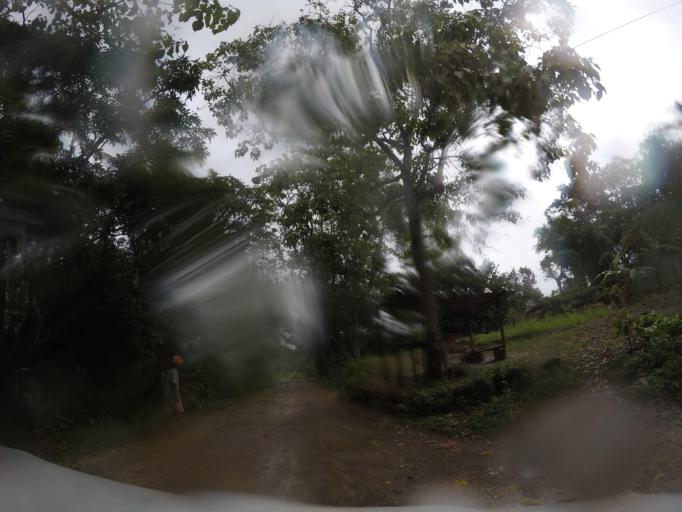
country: TL
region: Baucau
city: Venilale
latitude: -8.6414
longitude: 126.3819
